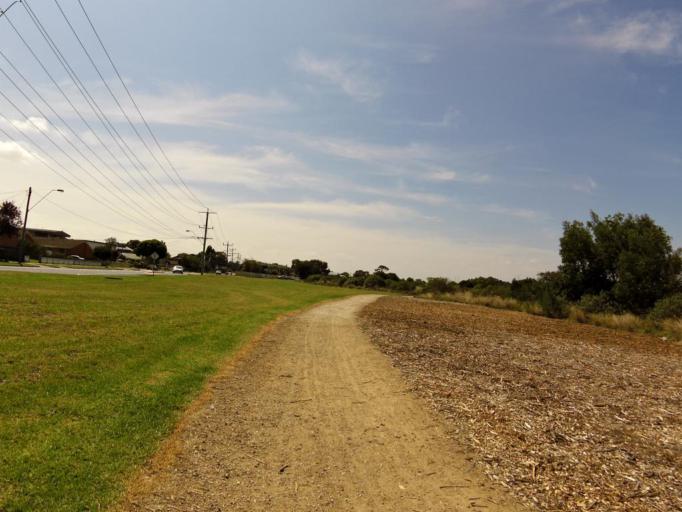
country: AU
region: Victoria
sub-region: Mornington Peninsula
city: Hastings
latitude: -38.3158
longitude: 145.1937
